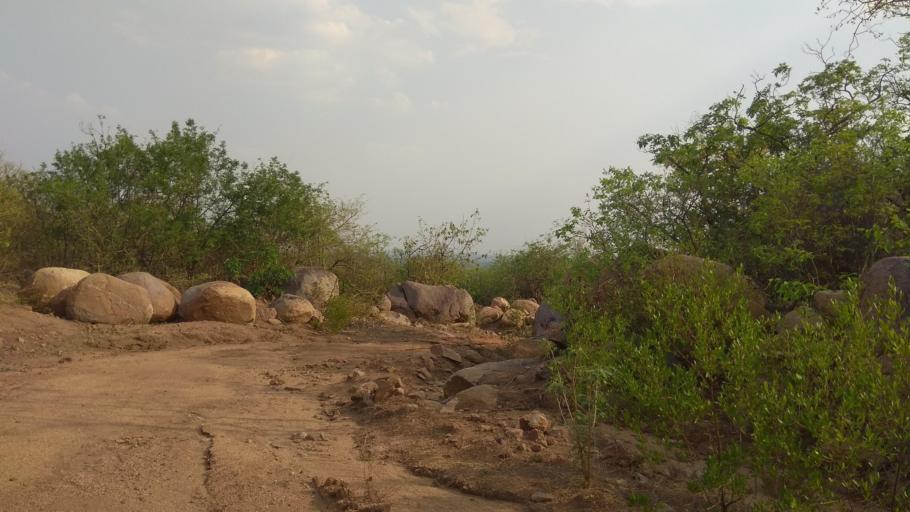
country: IN
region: Telangana
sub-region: Mahbubnagar
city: Farrukhnagar
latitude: 16.8937
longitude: 78.4969
